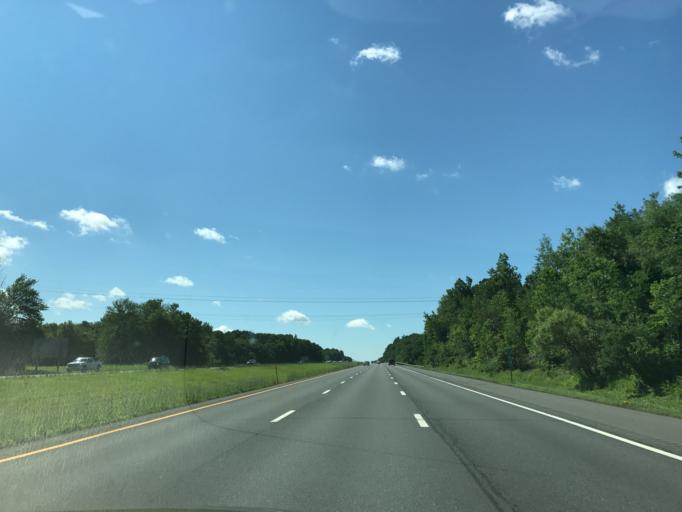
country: US
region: New York
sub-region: Rensselaer County
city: East Greenbush
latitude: 42.6179
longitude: -73.6907
